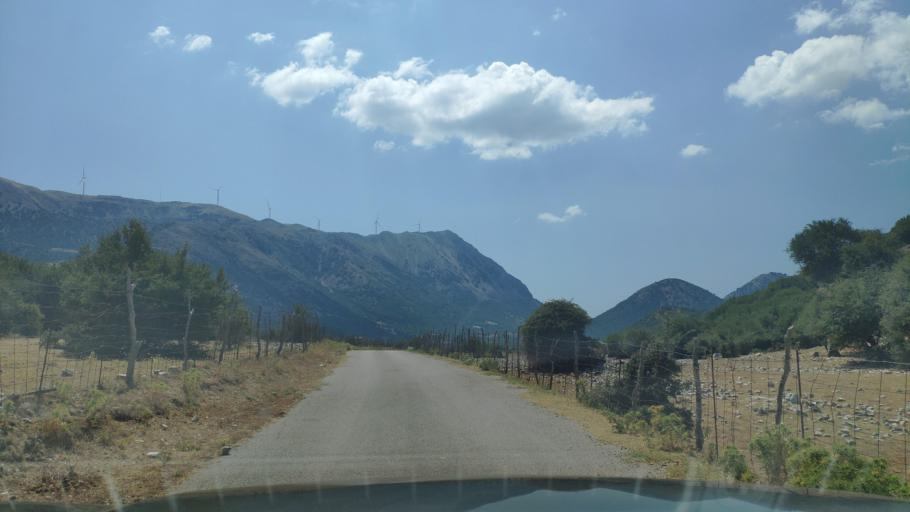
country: GR
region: West Greece
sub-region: Nomos Aitolias kai Akarnanias
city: Monastirakion
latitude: 38.7947
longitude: 20.9585
